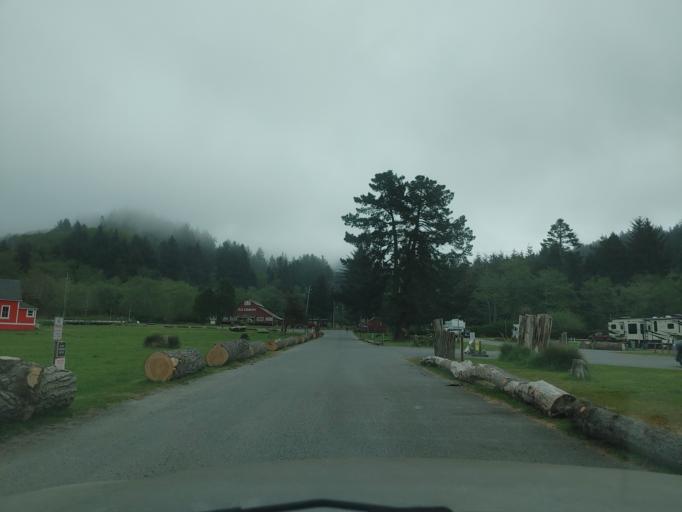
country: US
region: California
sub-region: Humboldt County
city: Westhaven-Moonstone
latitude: 41.2238
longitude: -124.0898
